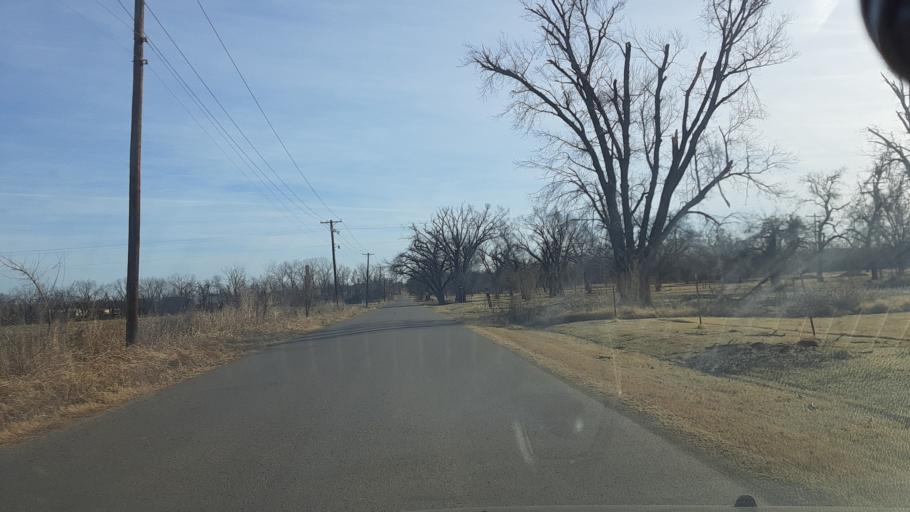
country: US
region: Oklahoma
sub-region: Logan County
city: Guthrie
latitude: 35.8853
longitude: -97.4351
